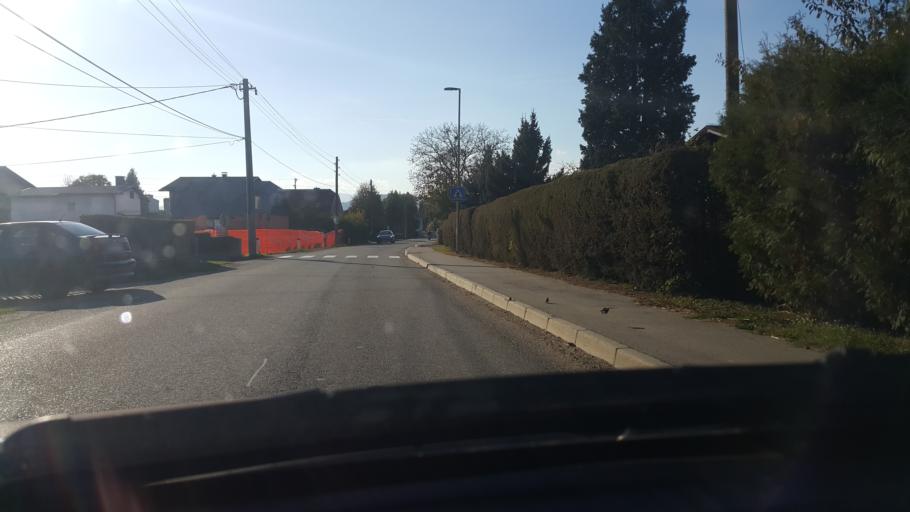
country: SI
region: Race-Fram
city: Race
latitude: 46.4522
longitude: 15.6858
